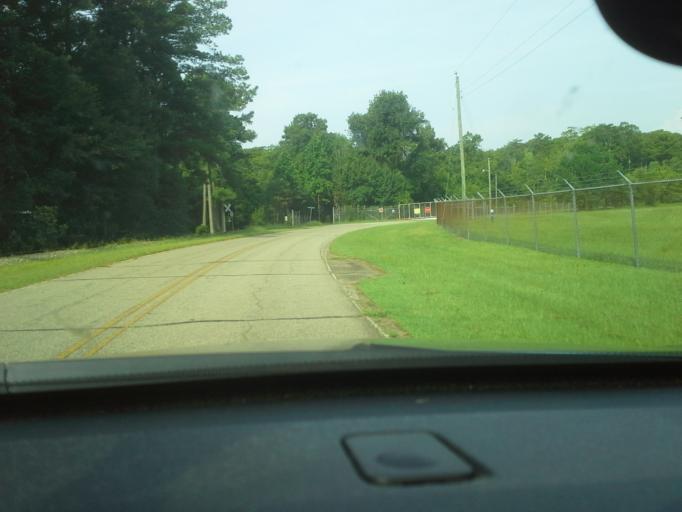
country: US
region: North Carolina
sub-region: Washington County
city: Plymouth
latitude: 35.8623
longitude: -76.7598
